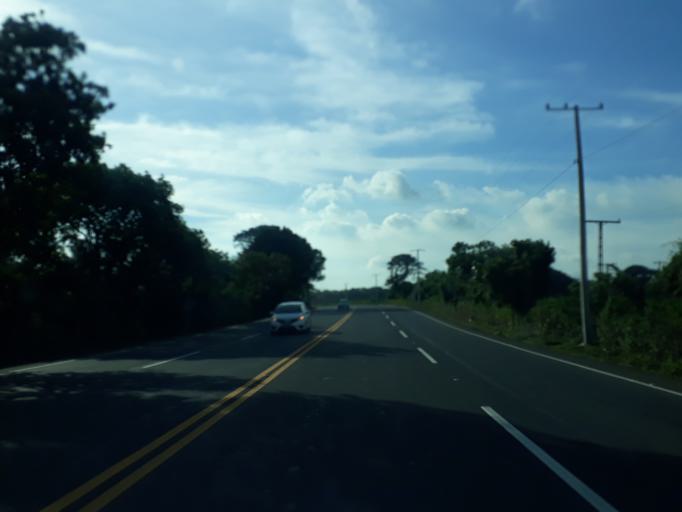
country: NI
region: Carazo
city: Diriamba
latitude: 11.9037
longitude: -86.2566
